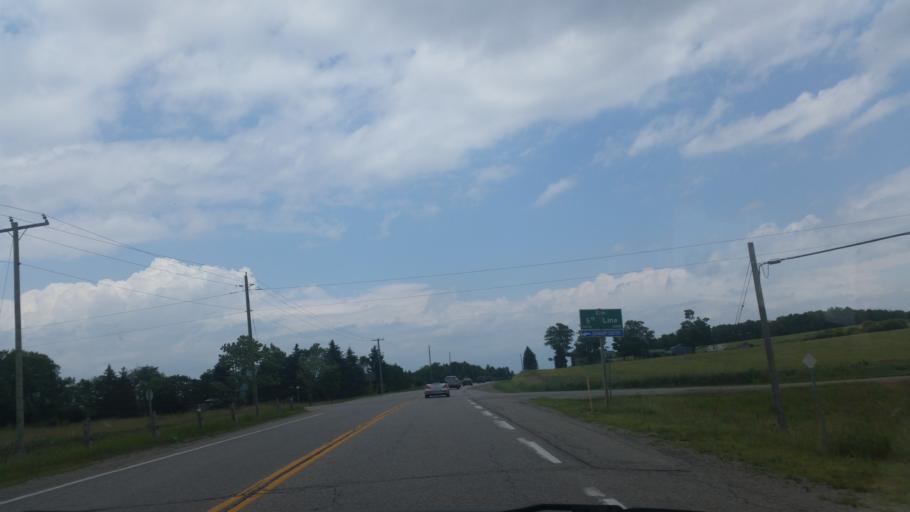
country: CA
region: Ontario
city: Orangeville
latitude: 43.7272
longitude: -80.1021
